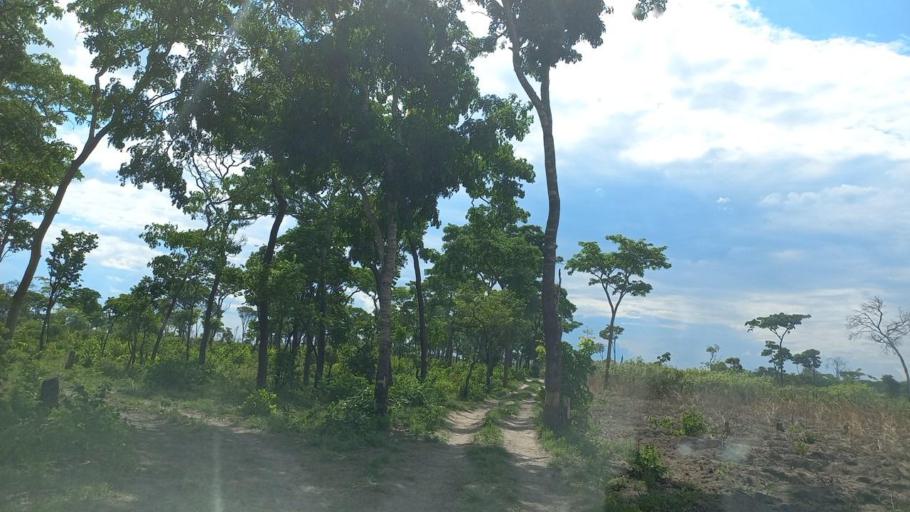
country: ZM
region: North-Western
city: Mufumbwe
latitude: -13.3398
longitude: 24.6317
